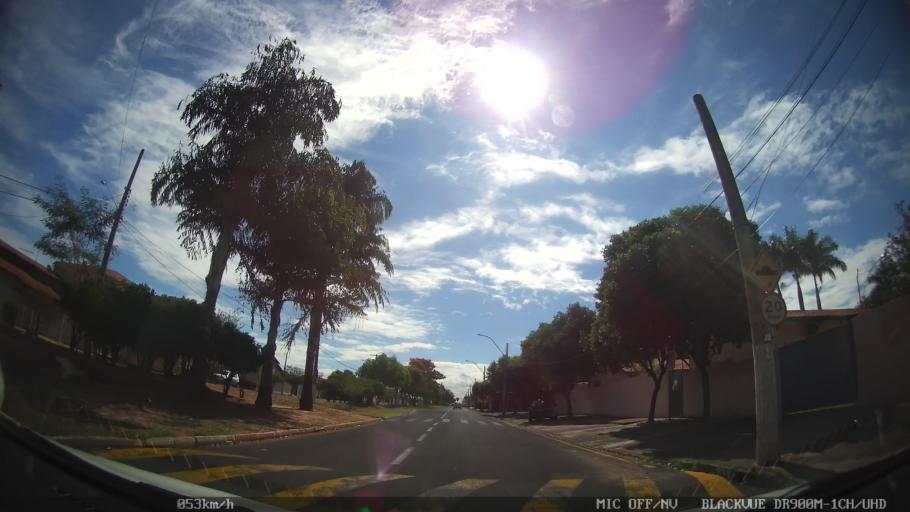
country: BR
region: Sao Paulo
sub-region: Bady Bassitt
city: Bady Bassitt
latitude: -20.8190
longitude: -49.4953
